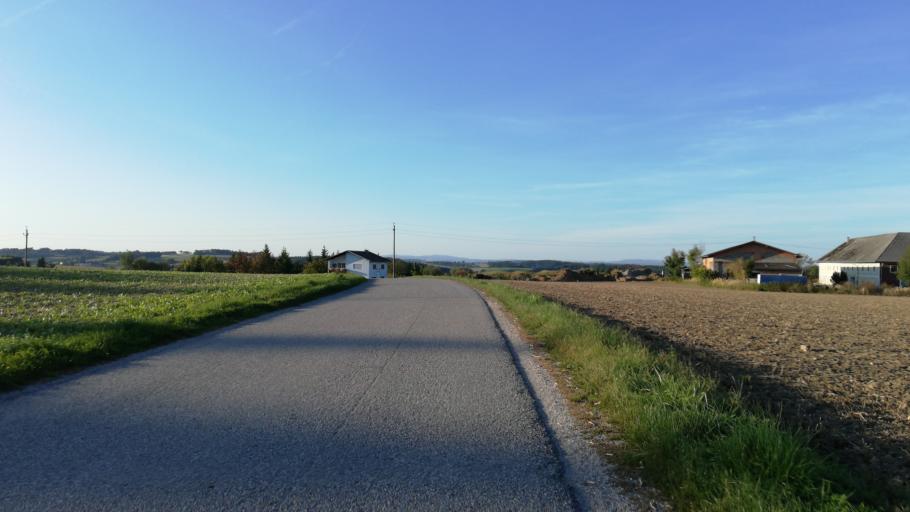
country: AT
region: Upper Austria
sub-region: Wels-Land
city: Offenhausen
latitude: 48.1637
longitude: 13.8589
